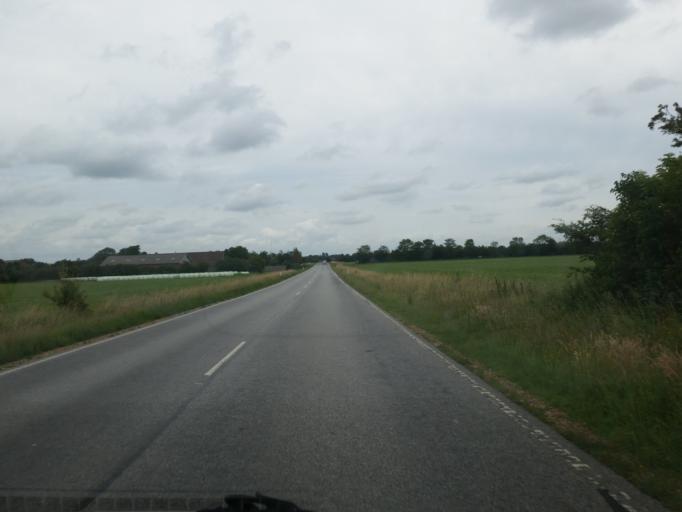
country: DK
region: South Denmark
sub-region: Vejen Kommune
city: Holsted
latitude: 55.3957
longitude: 8.9026
